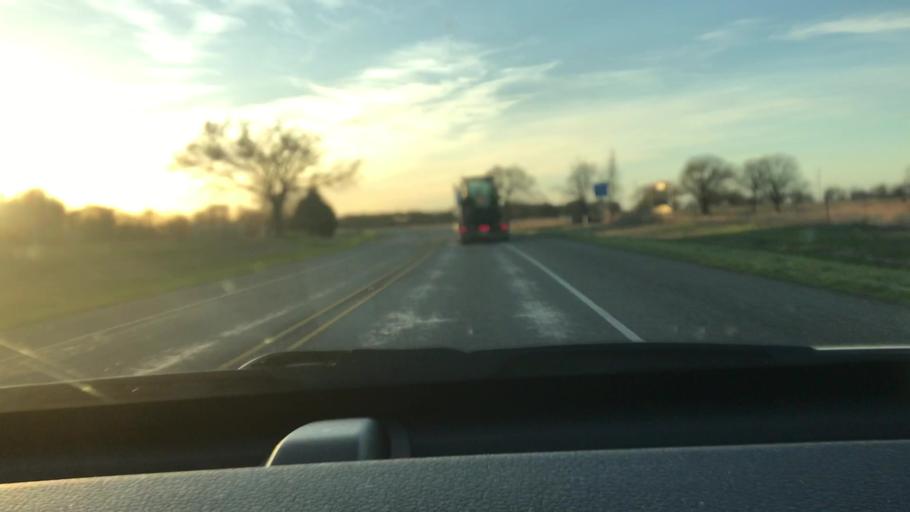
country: US
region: Texas
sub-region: Lamar County
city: Blossom
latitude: 33.6637
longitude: -95.3118
